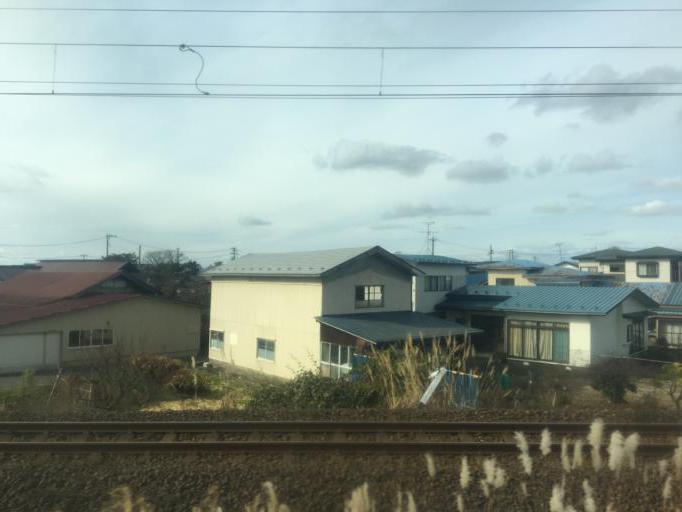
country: JP
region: Akita
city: Tenno
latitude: 39.9153
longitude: 140.0764
